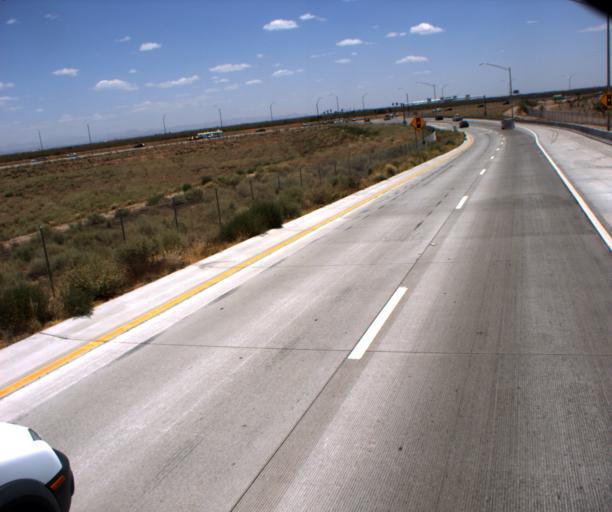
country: US
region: Arizona
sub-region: Maricopa County
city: Queen Creek
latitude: 33.3176
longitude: -111.6384
